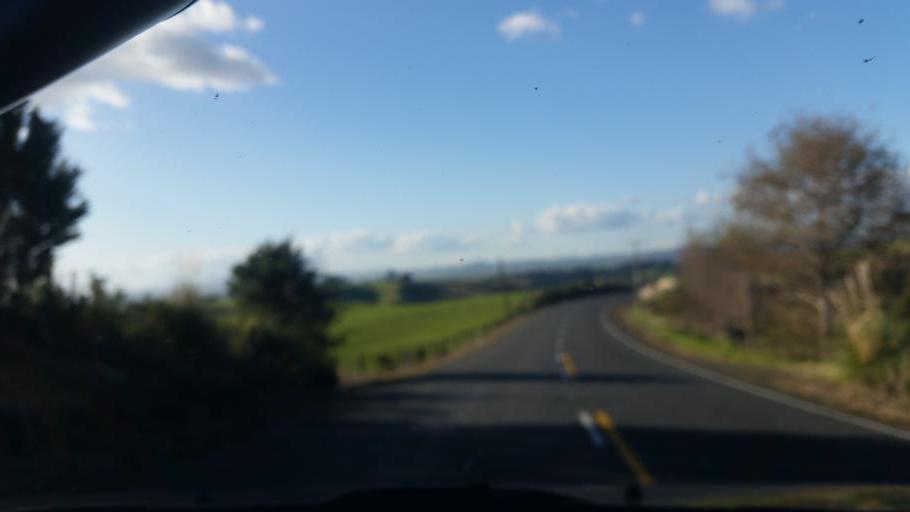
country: NZ
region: Northland
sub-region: Kaipara District
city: Dargaville
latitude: -36.2136
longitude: 174.0316
